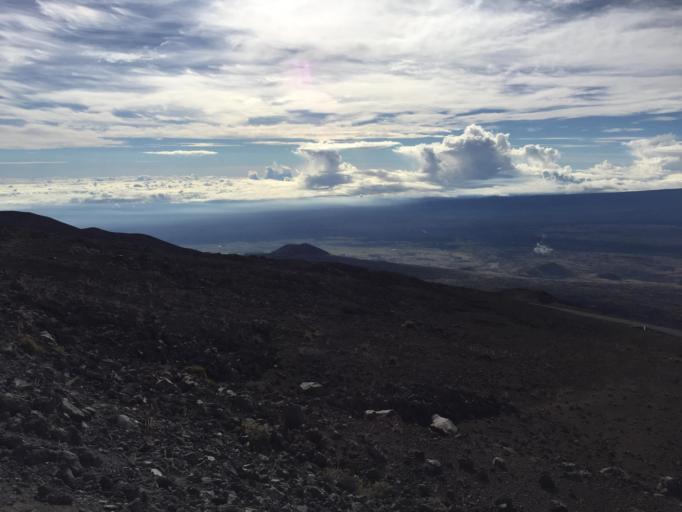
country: US
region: Hawaii
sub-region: Hawaii County
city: Honoka'a
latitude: 19.7764
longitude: -155.4537
